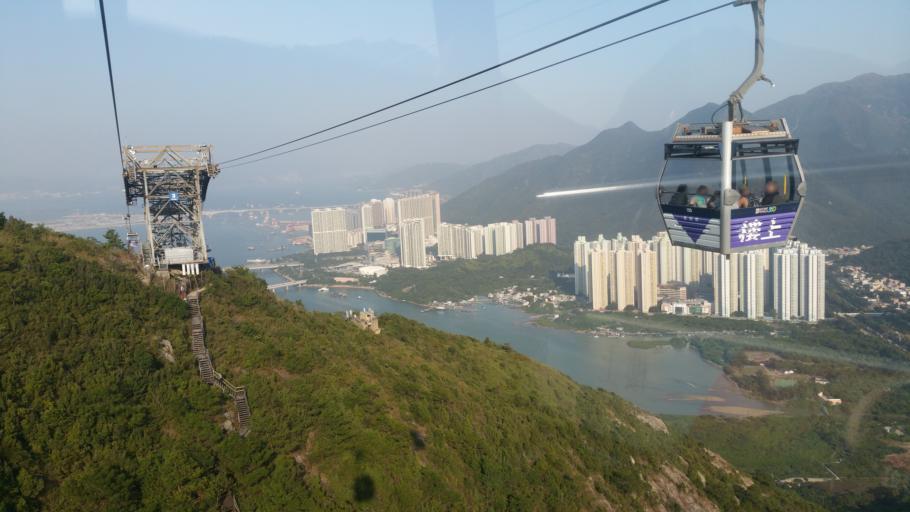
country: HK
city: Tai O
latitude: 22.2805
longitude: 113.9202
